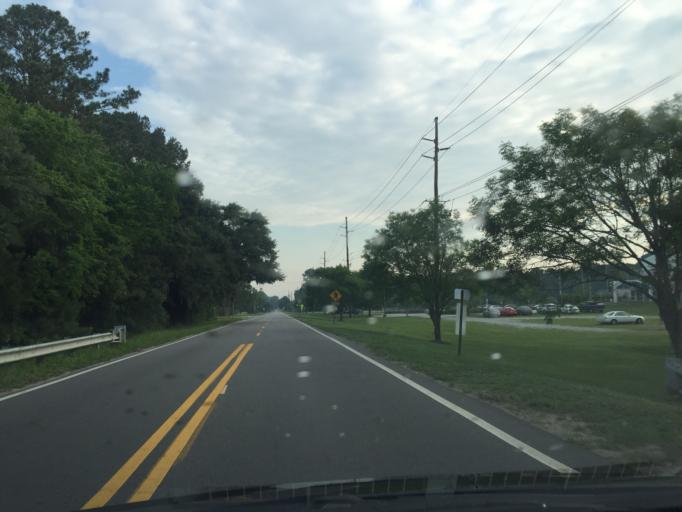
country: US
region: Georgia
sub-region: Chatham County
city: Isle of Hope
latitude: 31.9959
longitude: -81.0905
